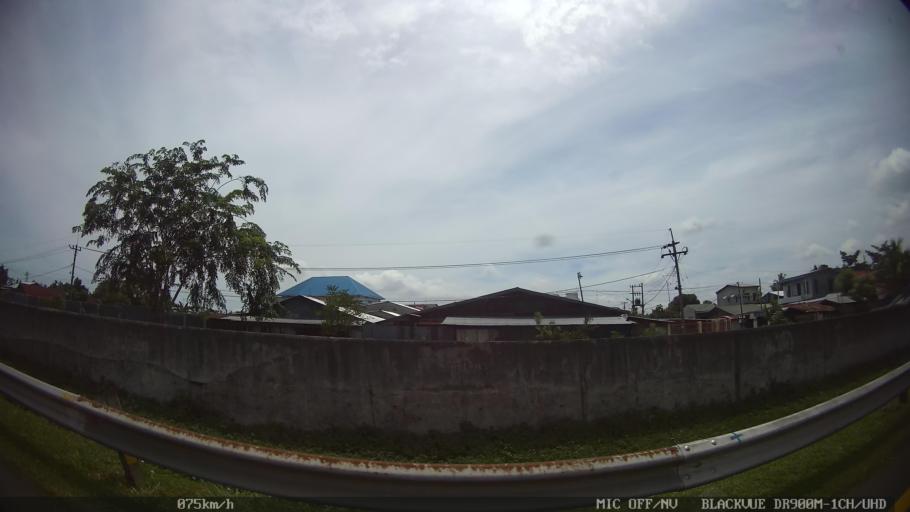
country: ID
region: North Sumatra
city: Labuhan Deli
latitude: 3.7179
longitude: 98.6827
